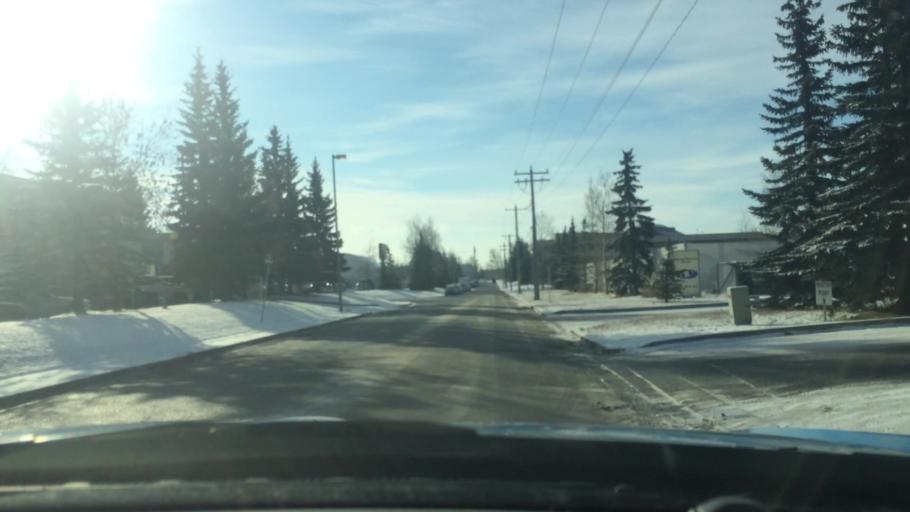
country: CA
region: Alberta
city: Calgary
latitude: 51.1166
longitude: -114.0447
